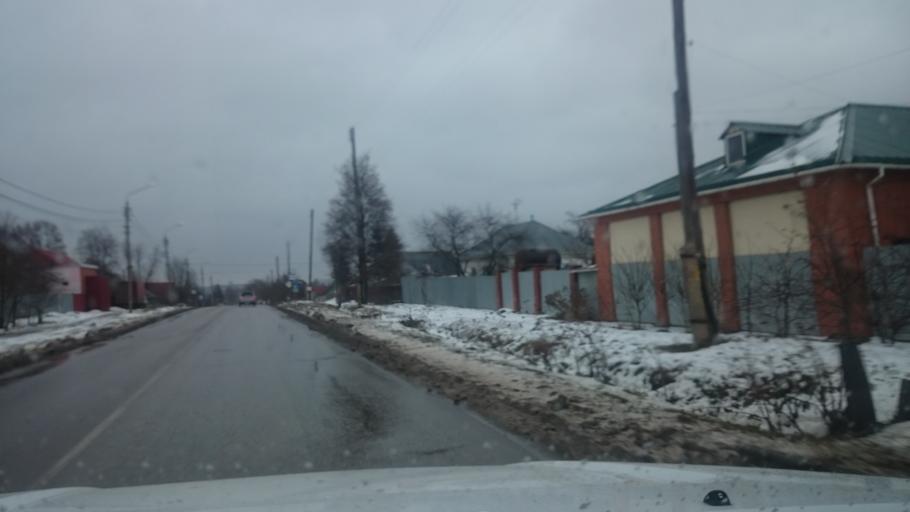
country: RU
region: Tula
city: Tula
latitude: 54.2011
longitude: 37.5516
